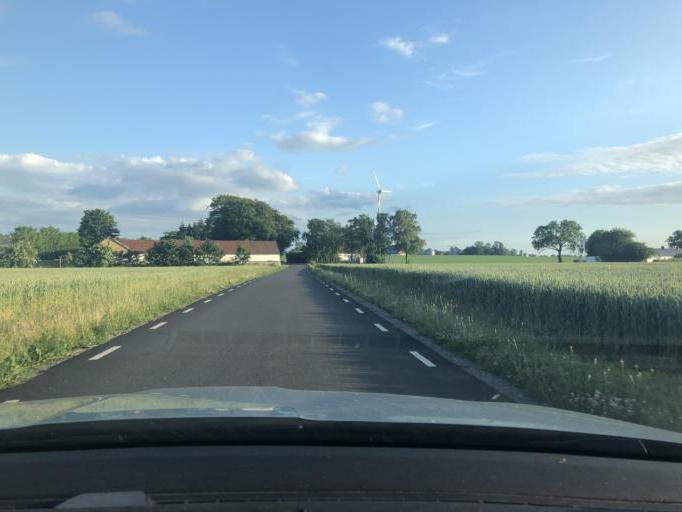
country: SE
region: Skane
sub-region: Simrishamns Kommun
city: Simrishamn
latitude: 55.4759
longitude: 14.1944
